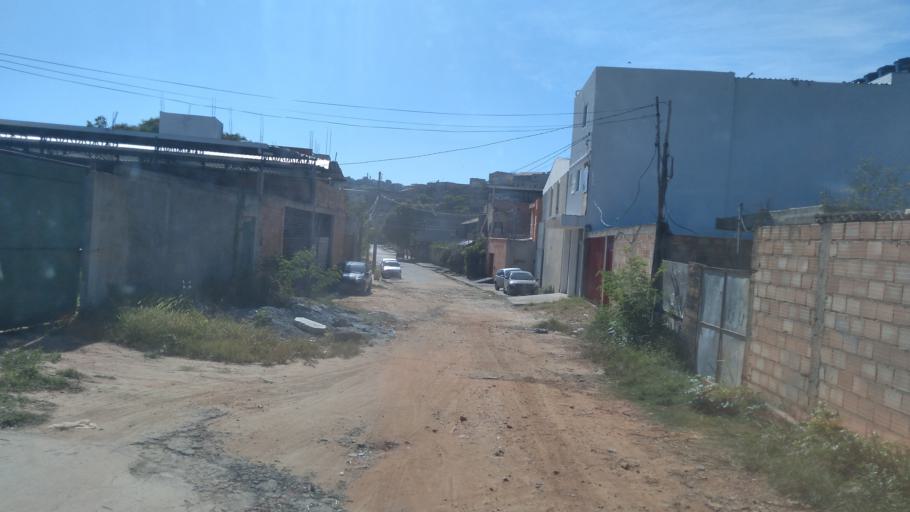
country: BR
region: Minas Gerais
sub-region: Belo Horizonte
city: Belo Horizonte
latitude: -19.8431
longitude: -43.9081
